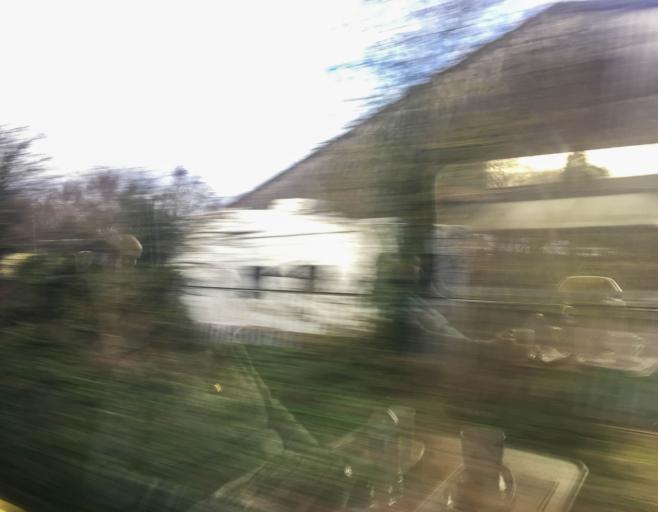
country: GB
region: Scotland
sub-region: Dumfries and Galloway
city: Gretna
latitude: 54.9968
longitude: -3.0437
